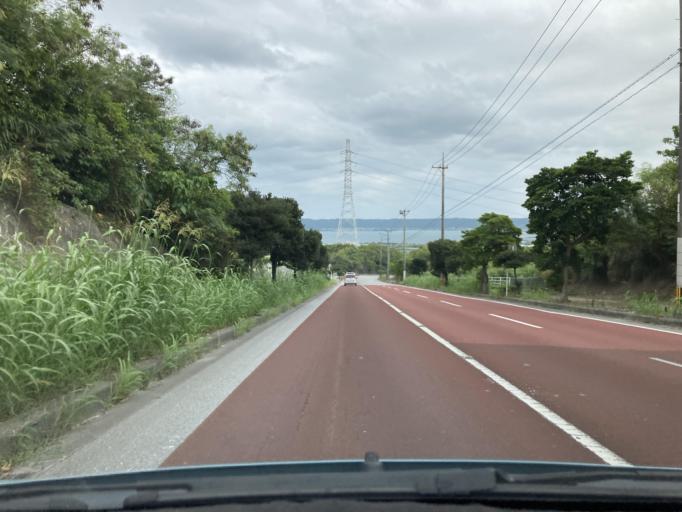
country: JP
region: Okinawa
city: Ginowan
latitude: 26.2382
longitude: 127.7655
